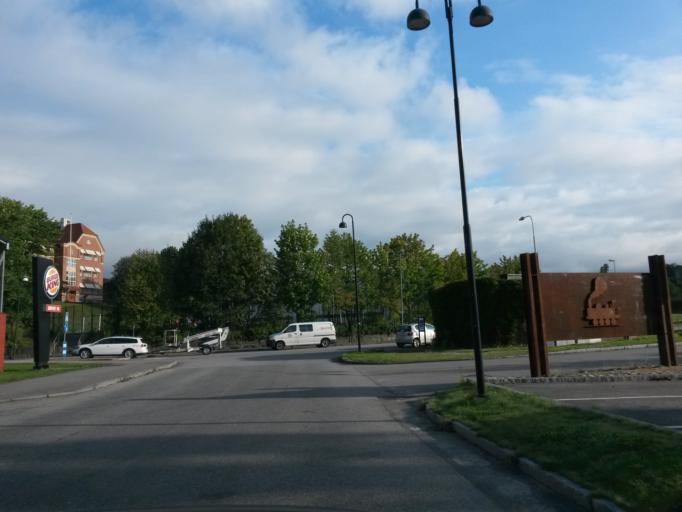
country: SE
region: Vaestra Goetaland
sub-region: Boras Kommun
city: Boras
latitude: 57.7106
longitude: 12.9458
